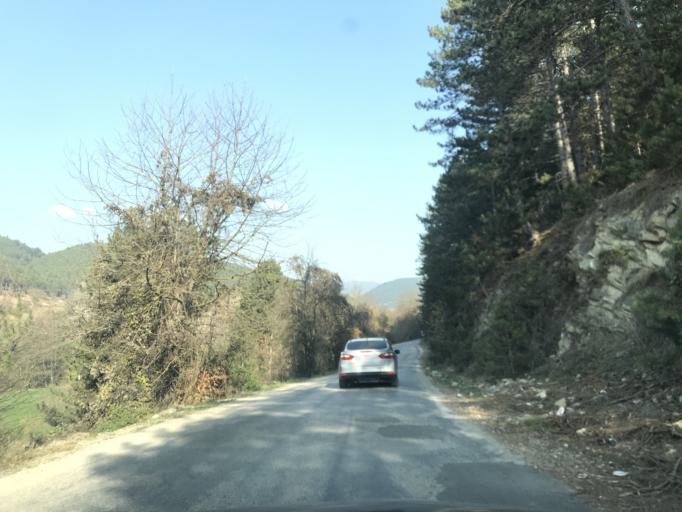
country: TR
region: Bolu
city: Bolu
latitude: 40.7886
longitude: 31.6366
